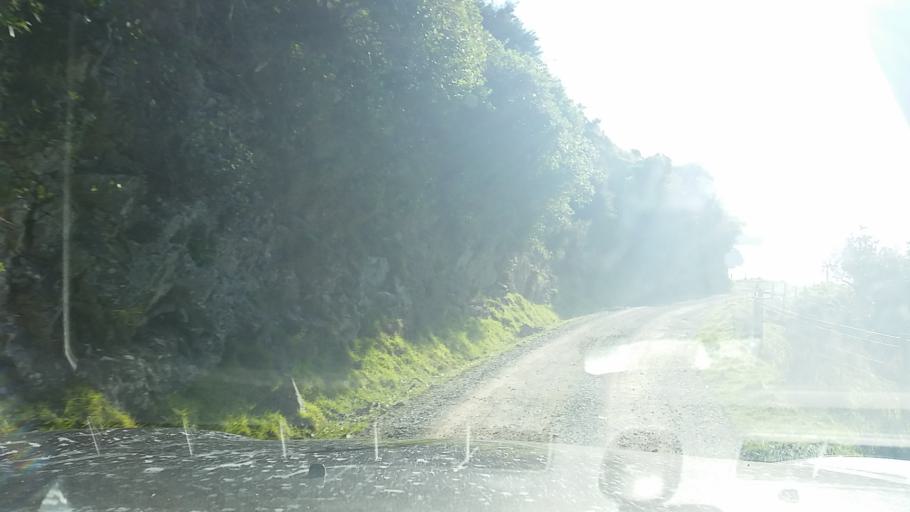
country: NZ
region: Marlborough
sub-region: Marlborough District
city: Picton
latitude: -41.0249
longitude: 174.1478
